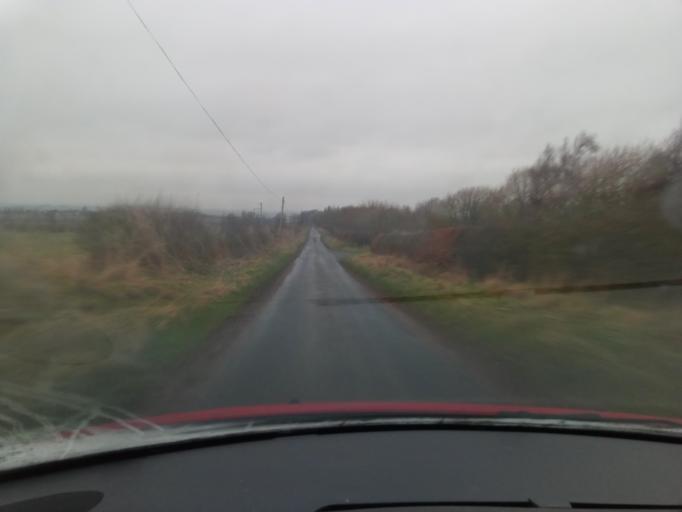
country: GB
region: Scotland
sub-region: The Scottish Borders
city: Kelso
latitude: 55.5643
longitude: -2.4343
